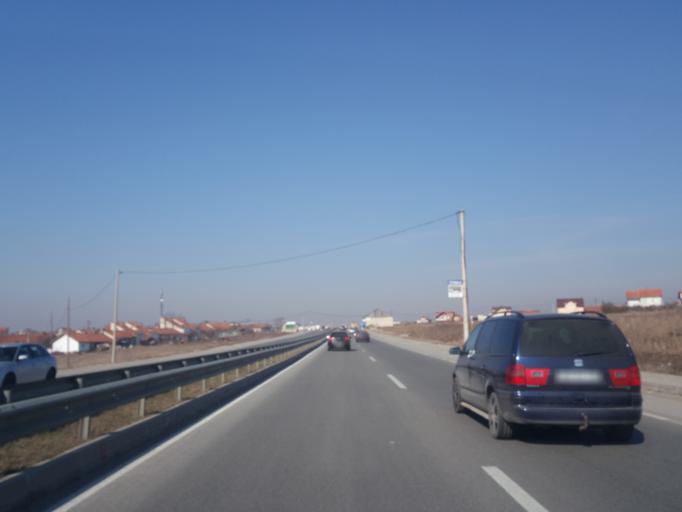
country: XK
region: Pristina
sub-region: Komuna e Obiliqit
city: Obiliq
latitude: 42.7567
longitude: 21.0348
